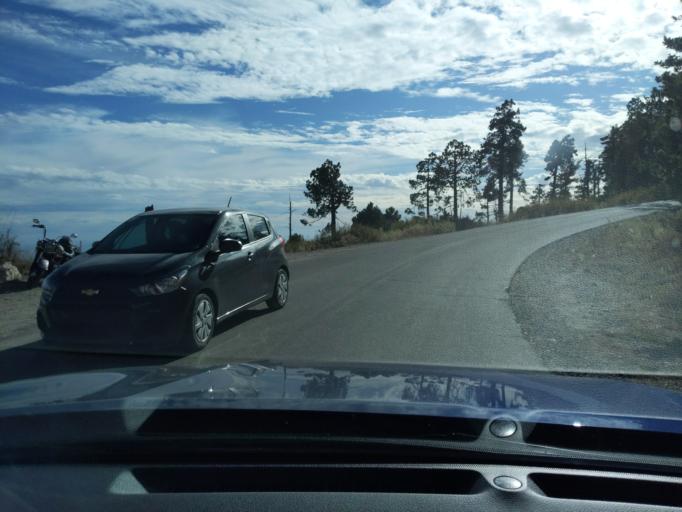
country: US
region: Arizona
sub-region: Pima County
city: Catalina
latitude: 32.4409
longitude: -110.7840
